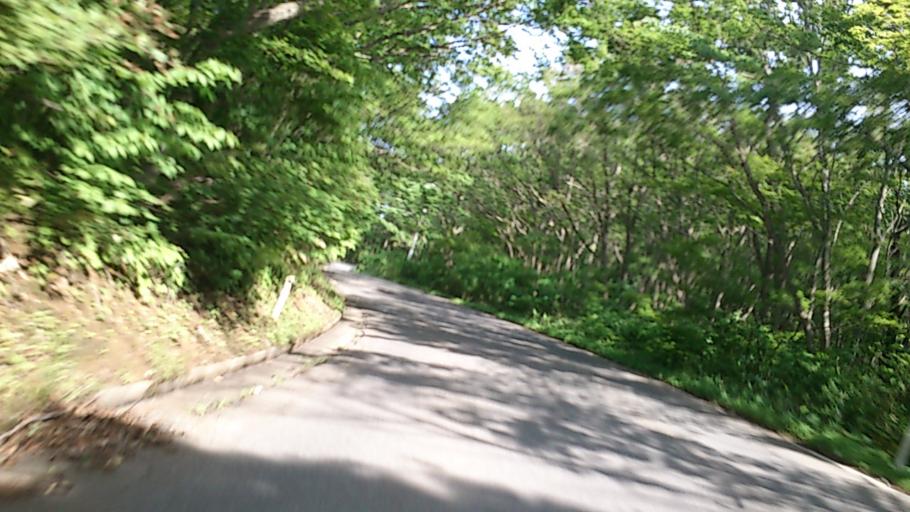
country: JP
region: Aomori
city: Aomori Shi
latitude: 40.7175
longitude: 140.8130
